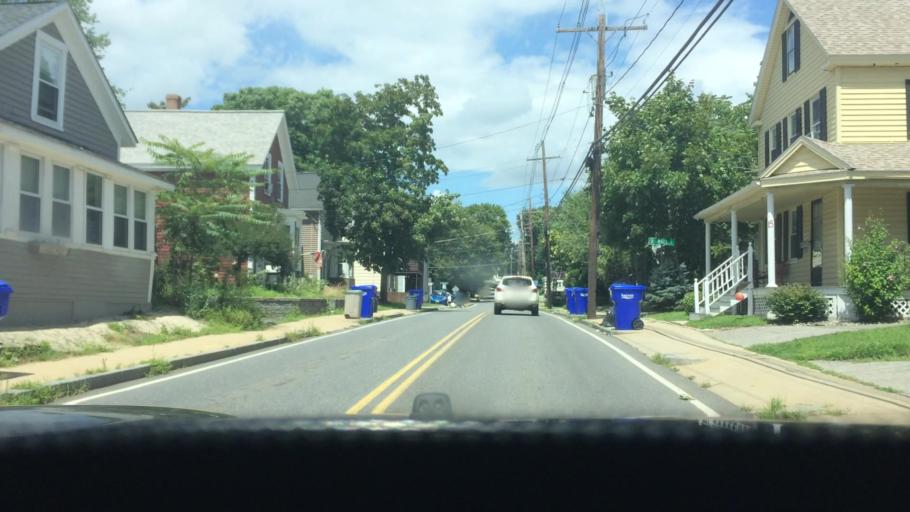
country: US
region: Massachusetts
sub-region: Middlesex County
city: Maynard
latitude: 42.4335
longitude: -71.4502
